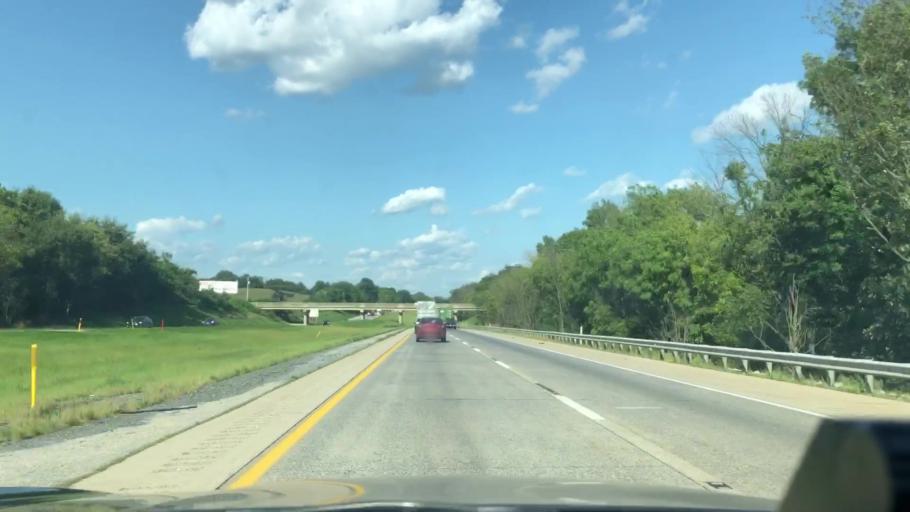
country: US
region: Pennsylvania
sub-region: Lebanon County
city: Palmyra
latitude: 40.3884
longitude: -76.6409
